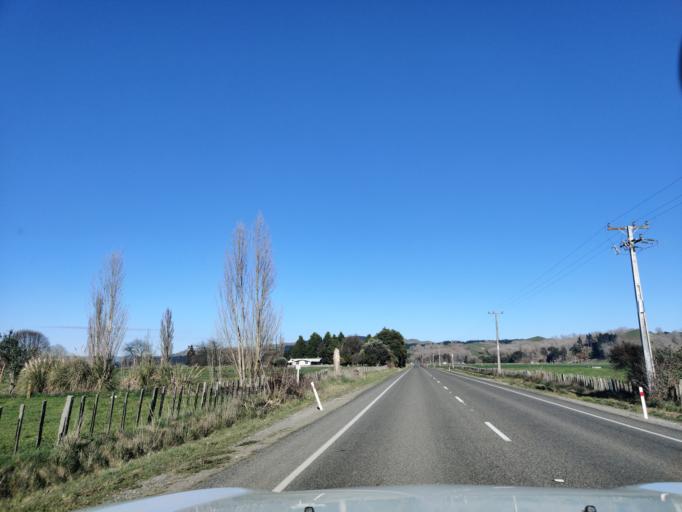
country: NZ
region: Manawatu-Wanganui
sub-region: Rangitikei District
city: Bulls
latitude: -39.9004
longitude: 175.6497
